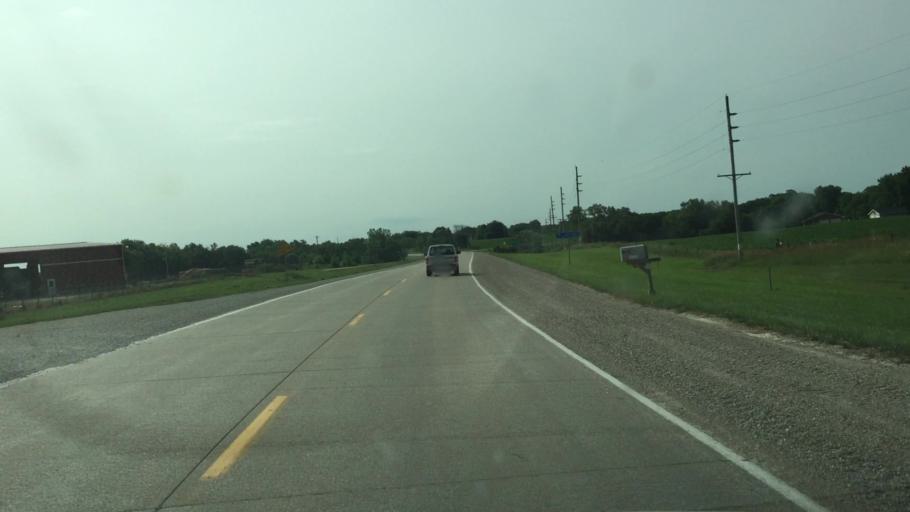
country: US
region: Illinois
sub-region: Hancock County
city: Nauvoo
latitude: 40.6368
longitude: -91.5192
